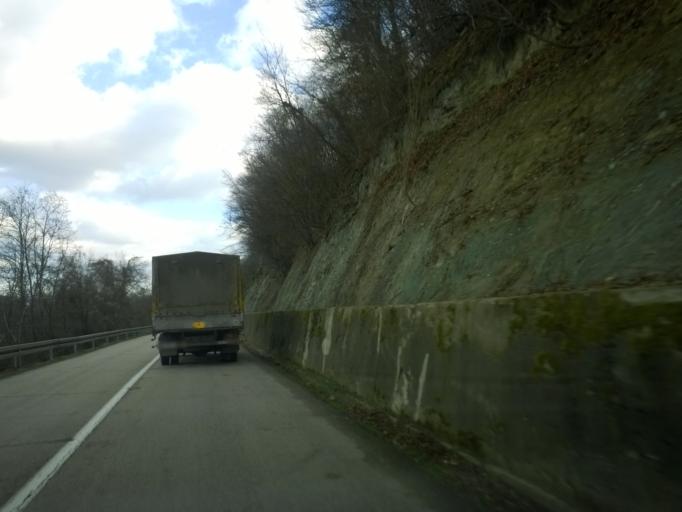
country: RO
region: Caras-Severin
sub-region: Comuna Berzasca
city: Liubcova
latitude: 44.6471
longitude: 21.8515
